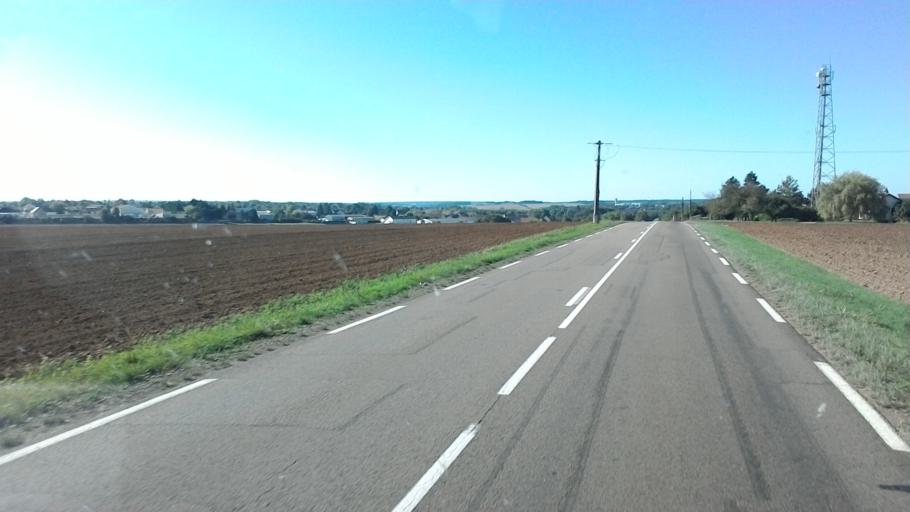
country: FR
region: Bourgogne
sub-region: Departement de la Cote-d'Or
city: Chatillon-sur-Seine
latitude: 47.8738
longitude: 4.5834
